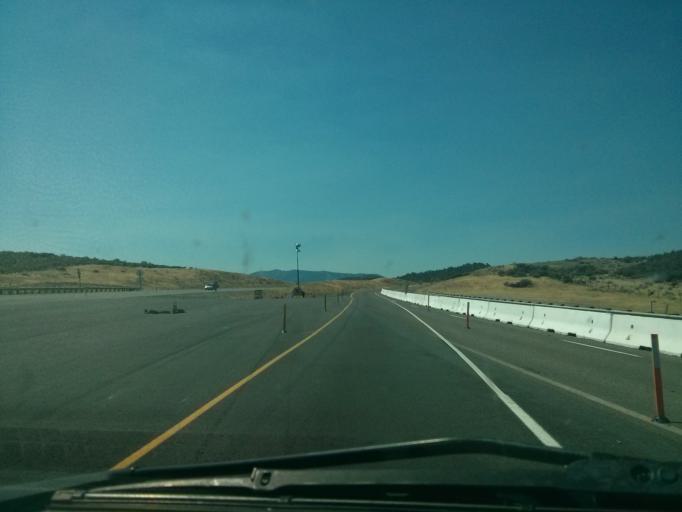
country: US
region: California
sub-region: Siskiyou County
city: Yreka
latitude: 41.7644
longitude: -122.5878
